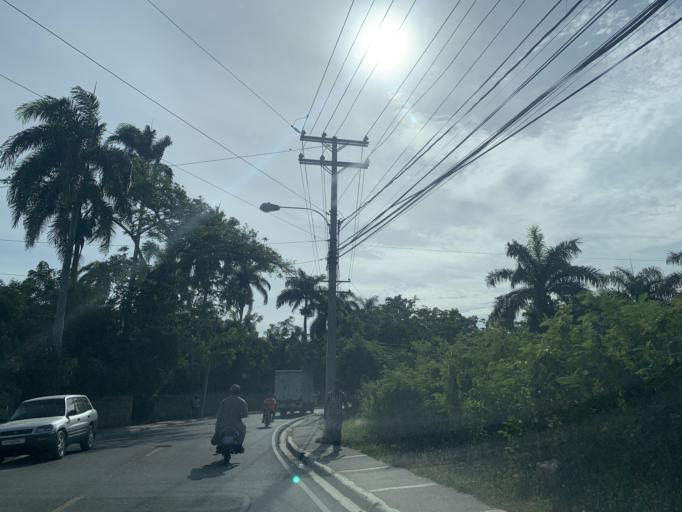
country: DO
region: Puerto Plata
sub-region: Puerto Plata
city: Puerto Plata
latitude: 19.8036
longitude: -70.7182
